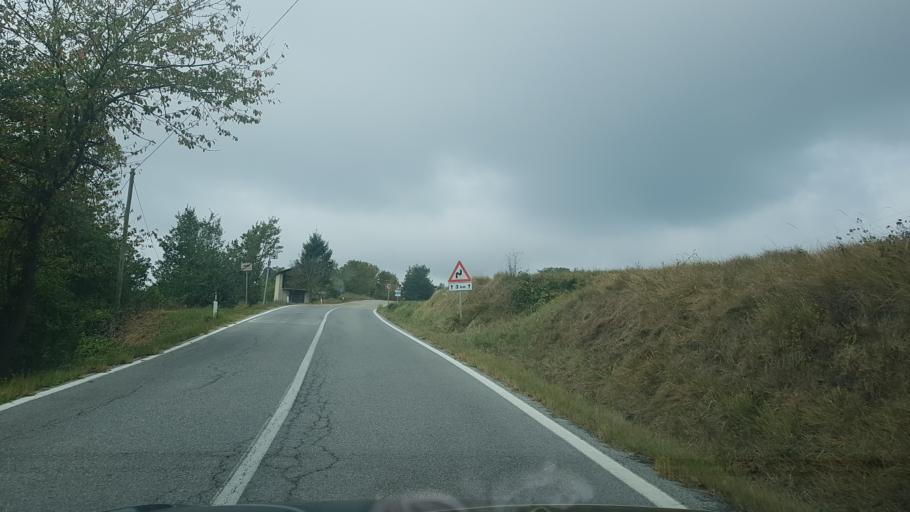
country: IT
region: Piedmont
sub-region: Provincia di Cuneo
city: Sale delle Langhe
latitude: 44.4096
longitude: 8.1034
